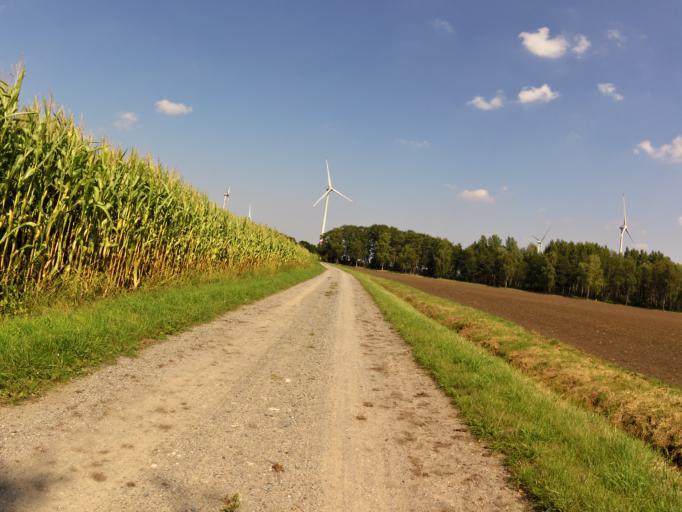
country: DE
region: North Rhine-Westphalia
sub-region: Regierungsbezirk Munster
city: Ahaus
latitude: 52.0199
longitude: 6.9907
